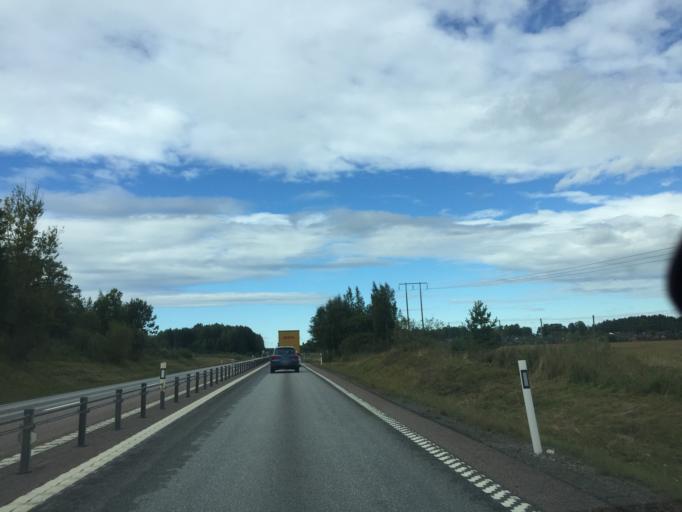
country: SE
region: Vaestmanland
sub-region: Kungsors Kommun
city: Kungsoer
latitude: 59.4126
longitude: 16.0816
